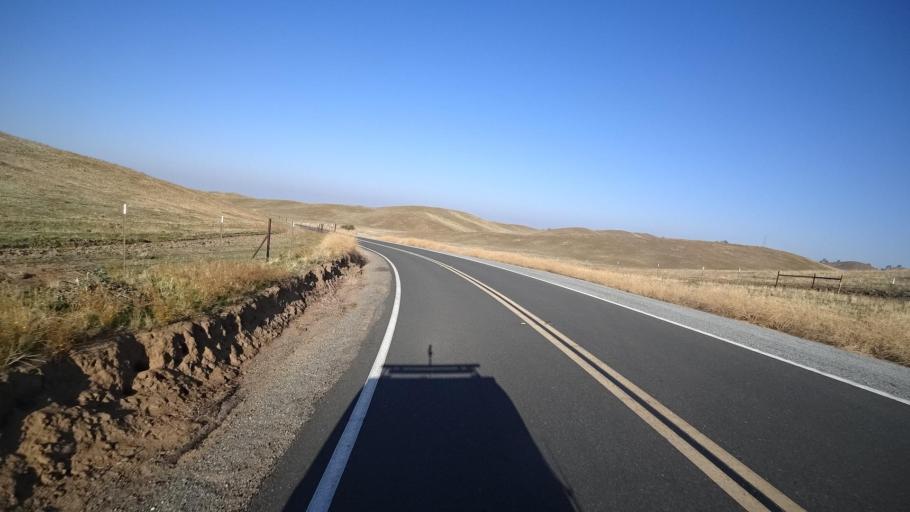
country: US
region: California
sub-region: Tulare County
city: Richgrove
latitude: 35.7437
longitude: -118.8790
